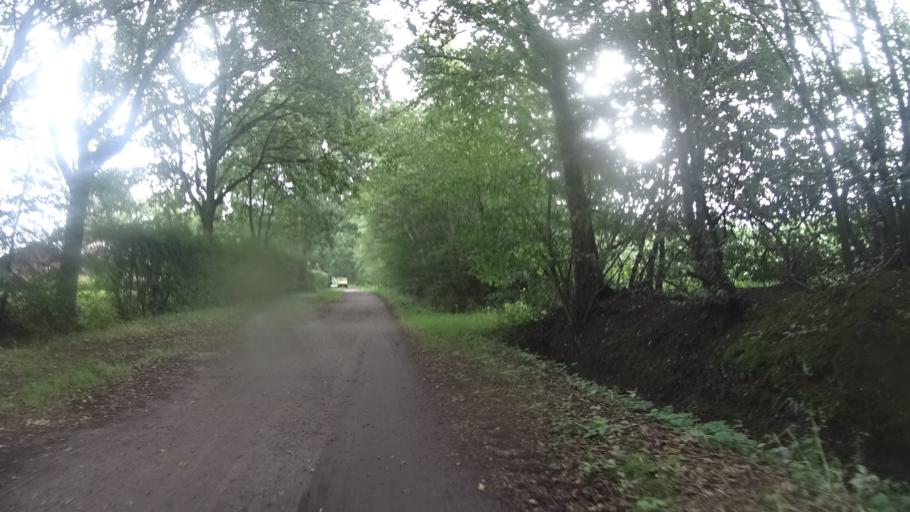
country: DE
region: Schleswig-Holstein
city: Hemdingen
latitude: 53.7668
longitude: 9.8390
